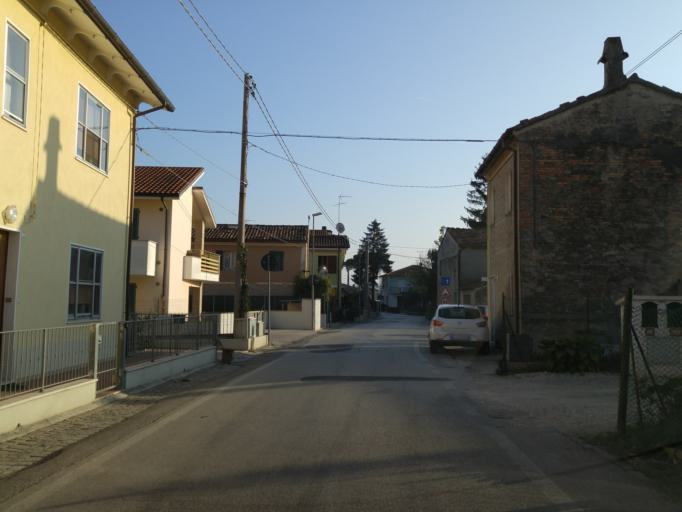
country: IT
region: The Marches
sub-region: Provincia di Pesaro e Urbino
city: Cuccurano
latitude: 43.8004
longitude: 12.9719
